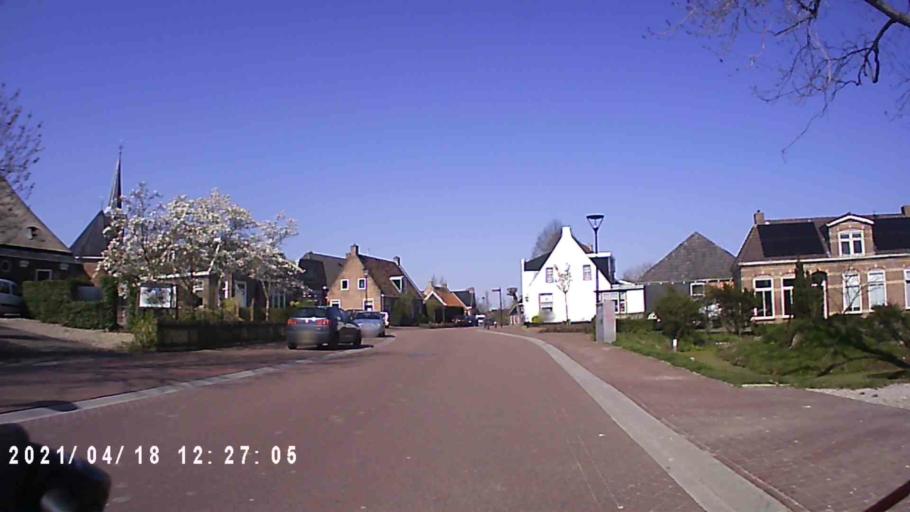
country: NL
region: Friesland
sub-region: Gemeente Dongeradeel
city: Anjum
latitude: 53.3309
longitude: 6.1025
